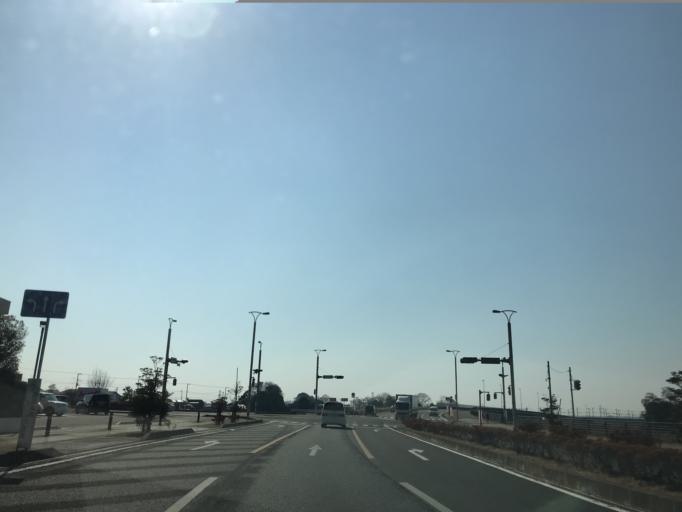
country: JP
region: Ibaraki
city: Mitsukaido
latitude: 35.9929
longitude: 140.0358
